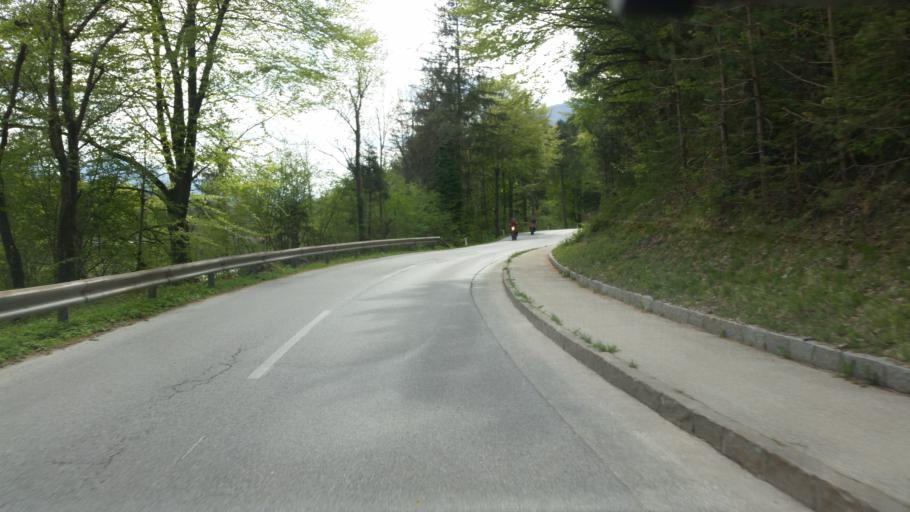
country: AT
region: Tyrol
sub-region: Politischer Bezirk Kufstein
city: Rattenberg
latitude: 47.4627
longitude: 11.8943
